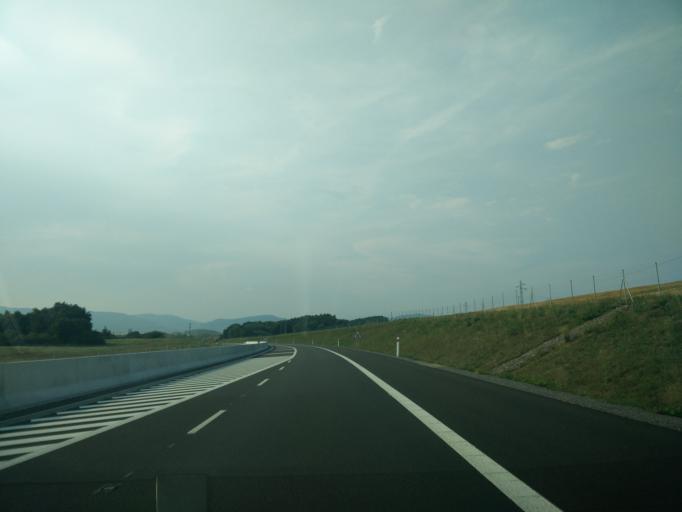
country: SK
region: Banskobystricky
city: Ziar nad Hronom
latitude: 48.5882
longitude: 18.8326
